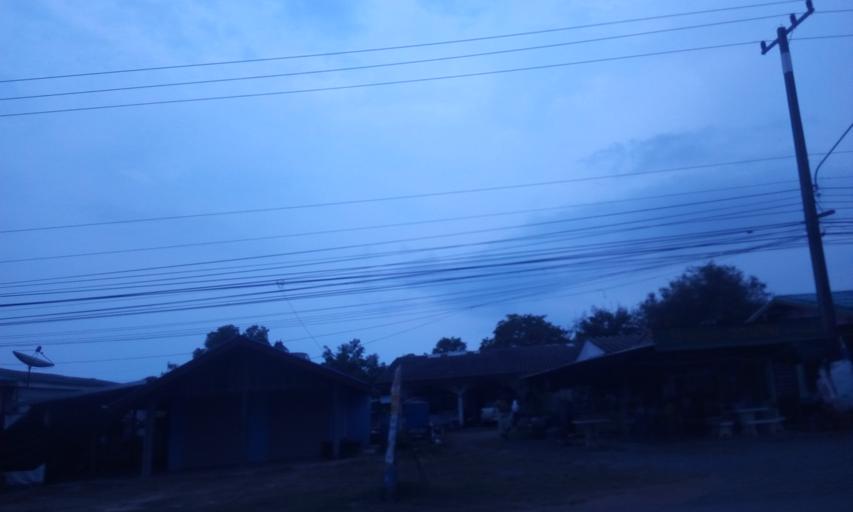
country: TH
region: Trat
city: Khao Saming
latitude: 12.4083
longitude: 102.3359
